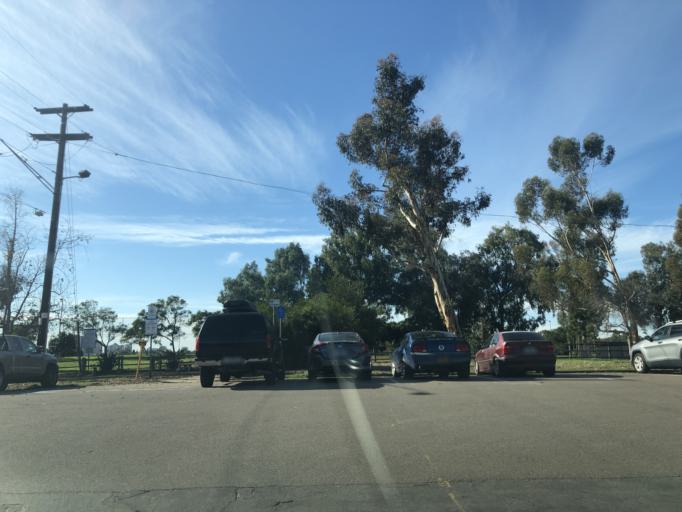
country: US
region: California
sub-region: San Diego County
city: San Diego
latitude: 32.7266
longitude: -117.1337
